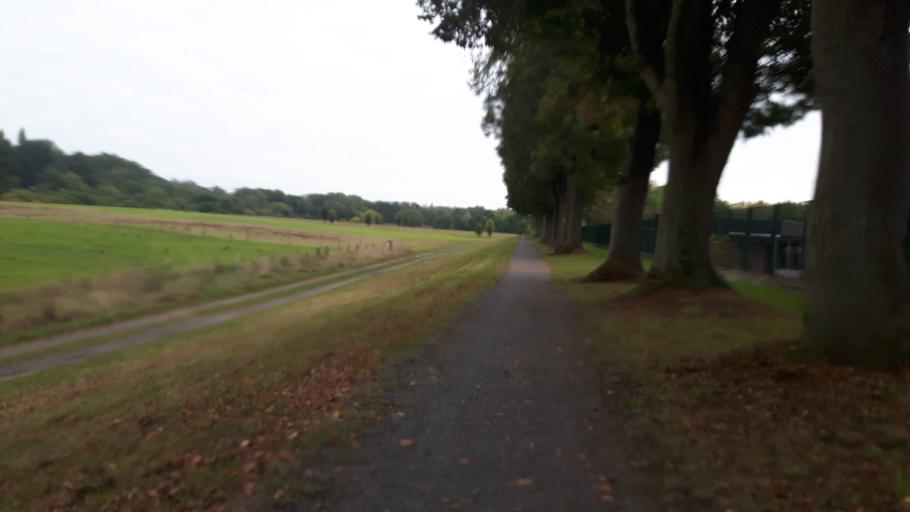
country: DE
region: North Rhine-Westphalia
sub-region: Regierungsbezirk Koln
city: Hennef
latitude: 50.7852
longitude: 7.2843
